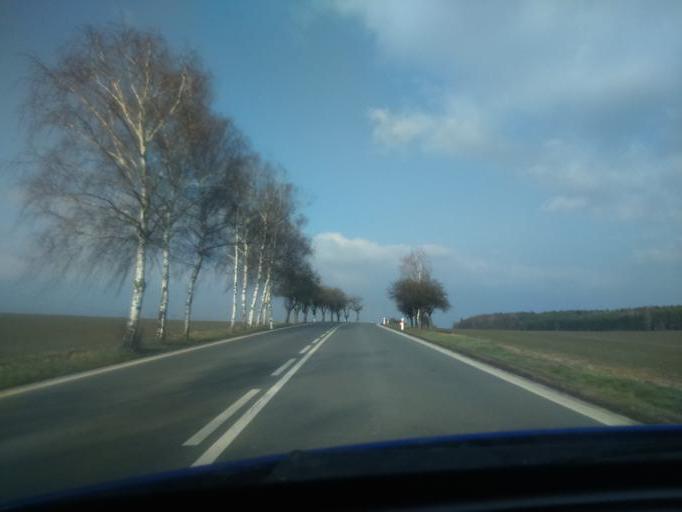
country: CZ
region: Plzensky
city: Holysov
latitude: 49.6155
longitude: 13.1330
